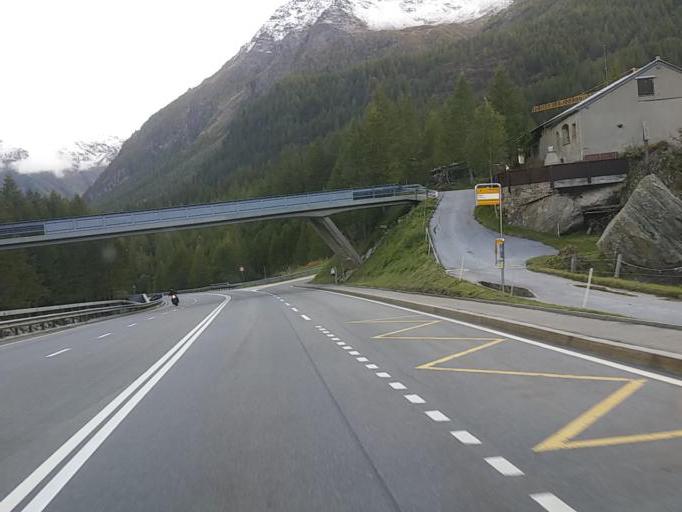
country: CH
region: Valais
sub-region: Brig District
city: Brig
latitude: 46.2053
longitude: 8.0431
